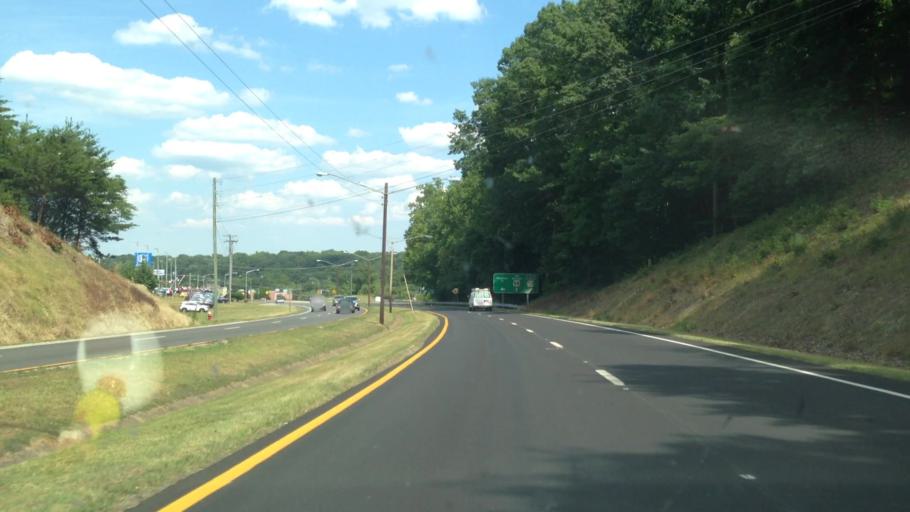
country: US
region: Virginia
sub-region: City of Danville
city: Danville
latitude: 36.5805
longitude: -79.4380
